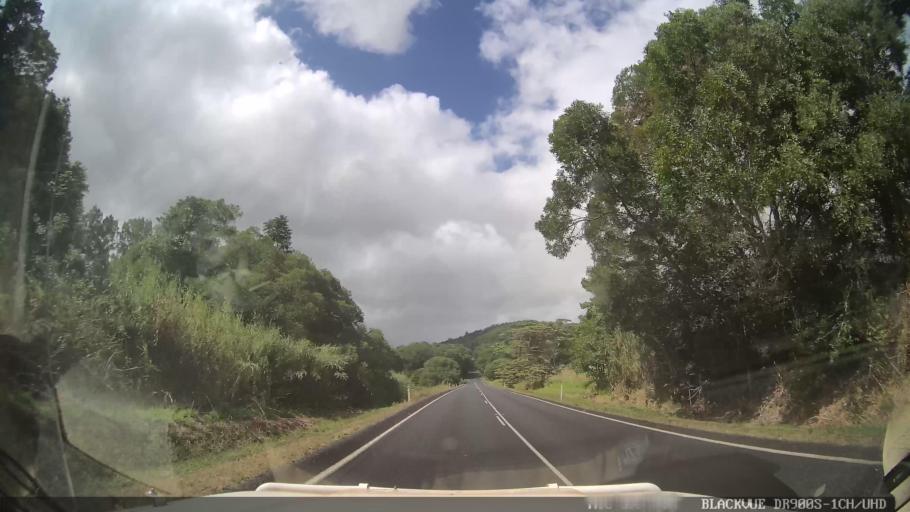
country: AU
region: Queensland
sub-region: Tablelands
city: Atherton
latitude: -17.3057
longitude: 145.6247
